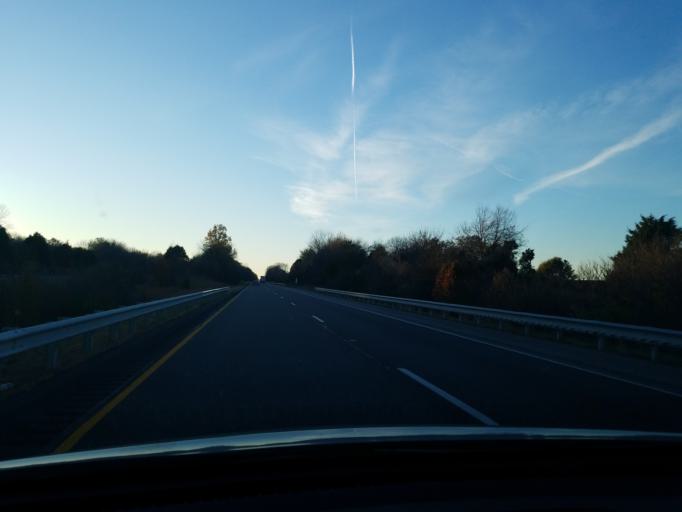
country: US
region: Indiana
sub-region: Gibson County
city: Haubstadt
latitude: 38.1671
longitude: -87.6038
